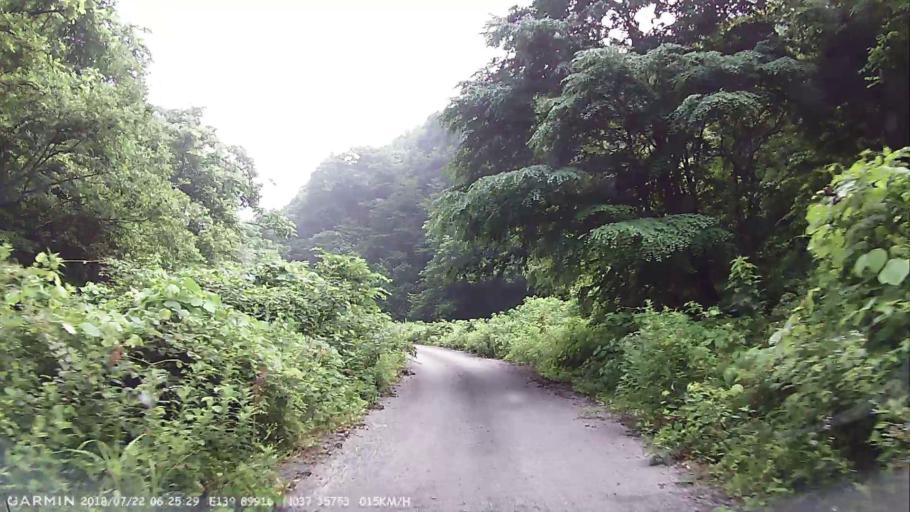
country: JP
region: Fukushima
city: Kitakata
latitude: 37.3576
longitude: 139.8992
